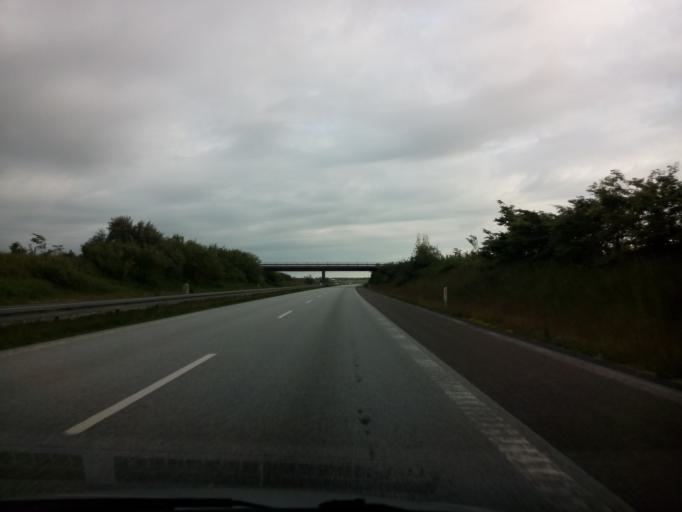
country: DK
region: North Denmark
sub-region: Hjorring Kommune
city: Hjorring
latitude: 57.3962
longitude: 10.0280
